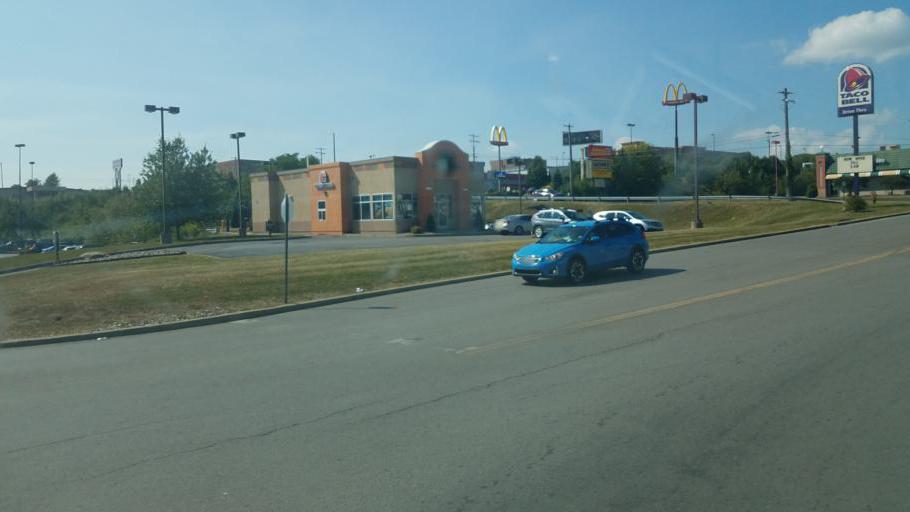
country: US
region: Pennsylvania
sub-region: Clarion County
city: Clarion
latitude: 41.1894
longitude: -79.3945
